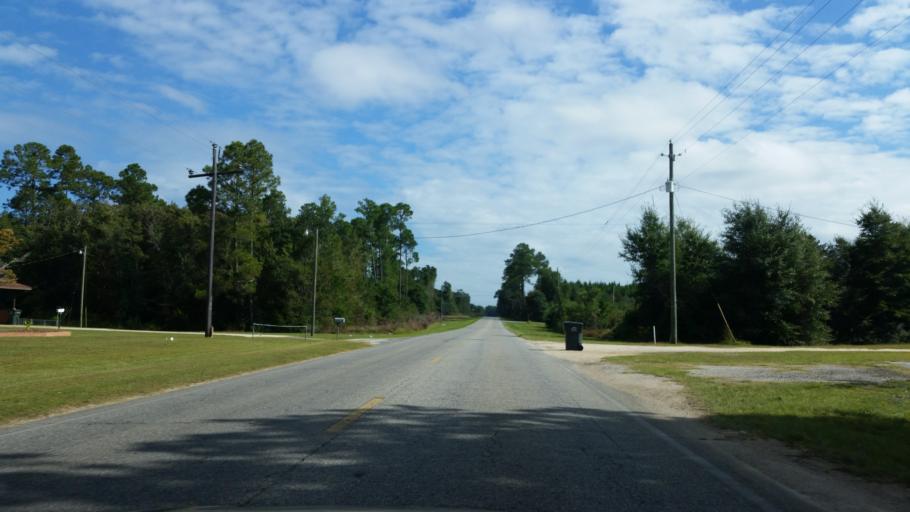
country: US
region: Florida
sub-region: Santa Rosa County
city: Milton
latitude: 30.6656
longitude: -87.0045
